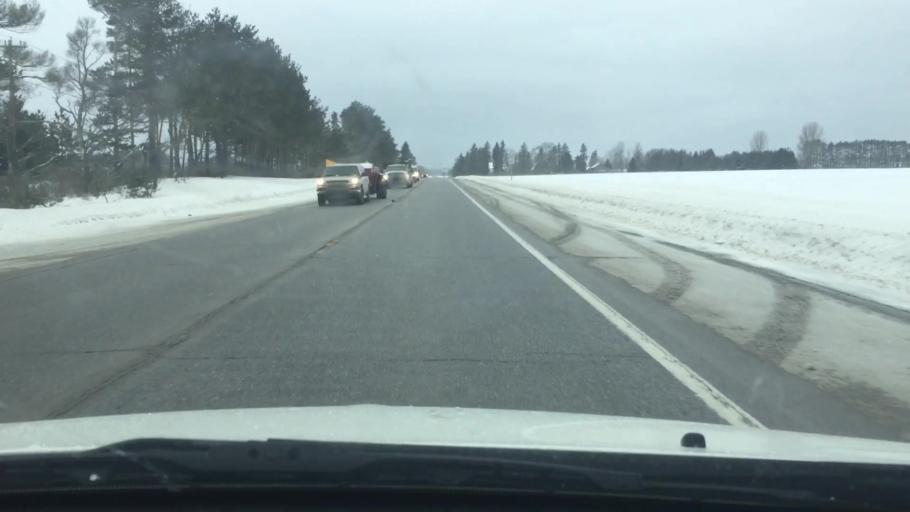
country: US
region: Michigan
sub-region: Otsego County
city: Gaylord
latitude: 45.0663
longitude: -84.8633
